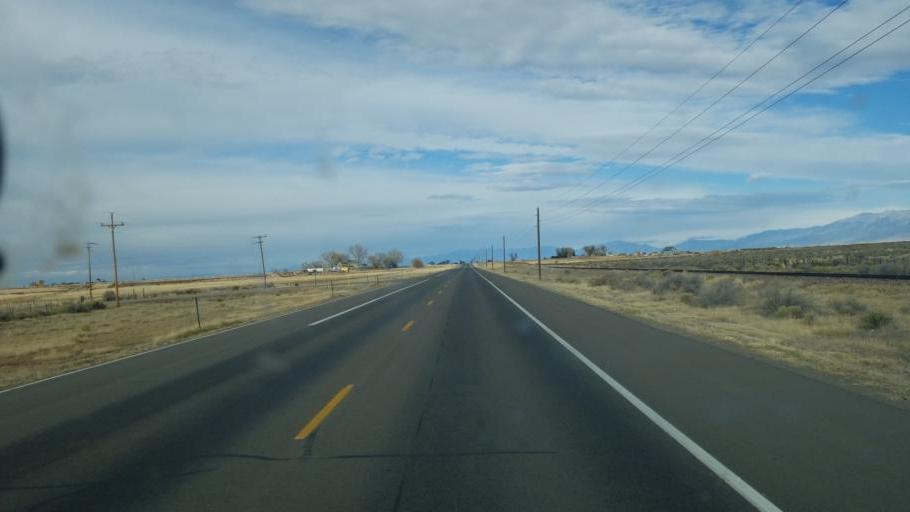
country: US
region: Colorado
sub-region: Alamosa County
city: Alamosa
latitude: 37.3406
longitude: -105.9379
